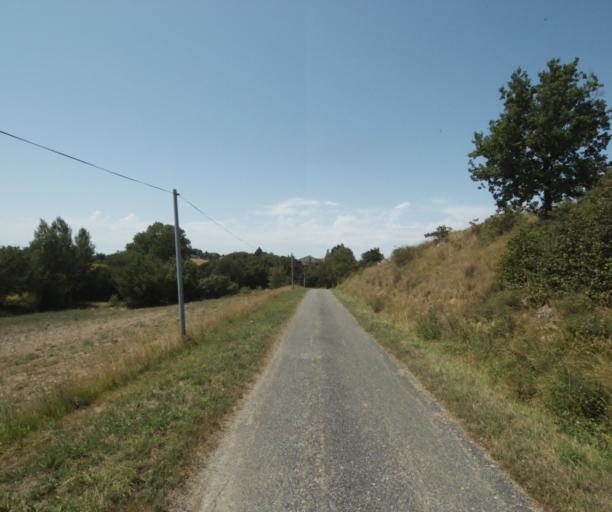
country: FR
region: Midi-Pyrenees
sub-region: Departement de la Haute-Garonne
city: Saint-Felix-Lauragais
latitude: 43.4550
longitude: 1.8477
